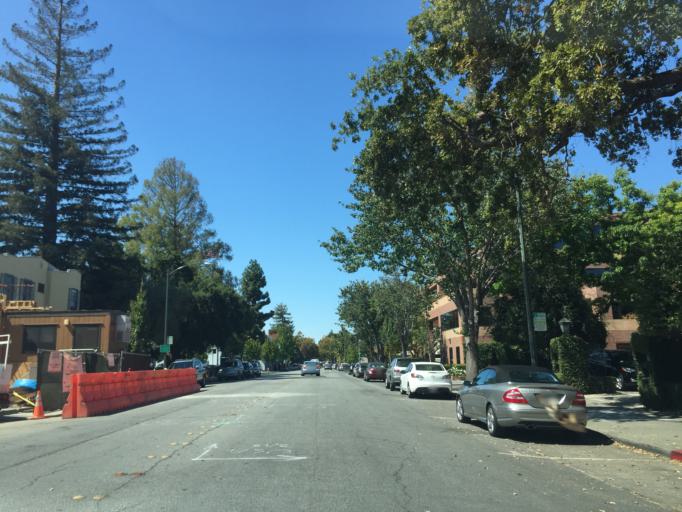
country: US
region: California
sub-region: Santa Clara County
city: Palo Alto
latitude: 37.4457
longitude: -122.1582
